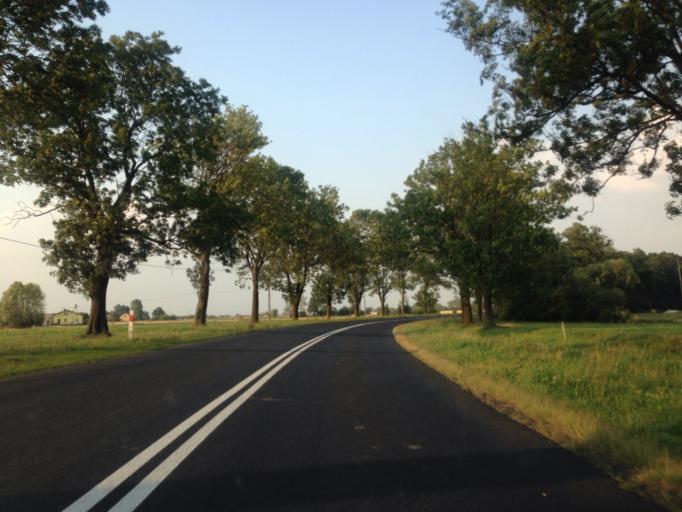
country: PL
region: Kujawsko-Pomorskie
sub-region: Powiat lipnowski
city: Lipno
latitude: 52.8966
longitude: 19.2124
